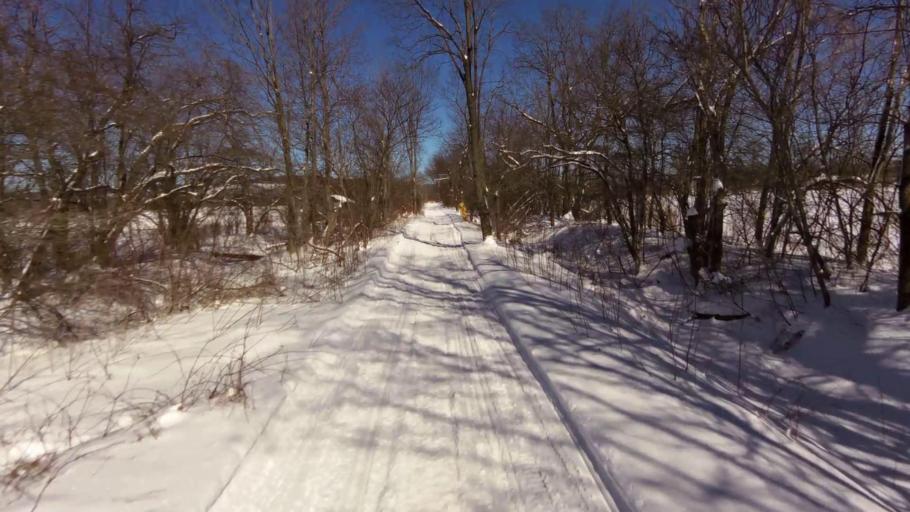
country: US
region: New York
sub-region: Chautauqua County
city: Celoron
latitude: 42.2447
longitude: -79.2683
